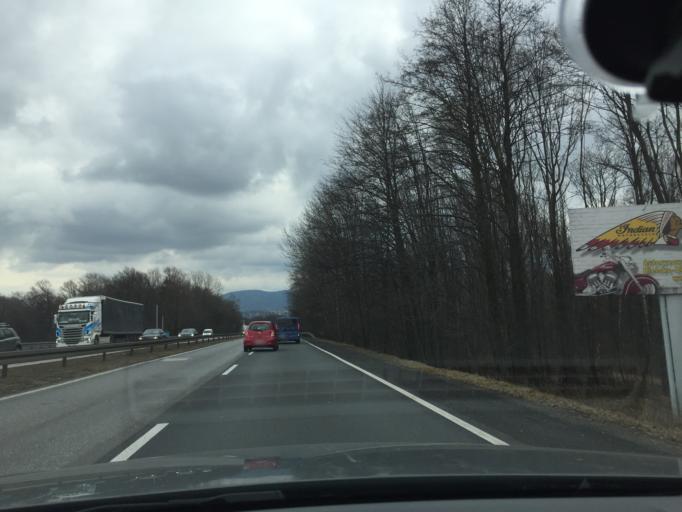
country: PL
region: Silesian Voivodeship
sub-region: Powiat bielski
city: Mazancowice
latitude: 49.8617
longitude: 19.0180
